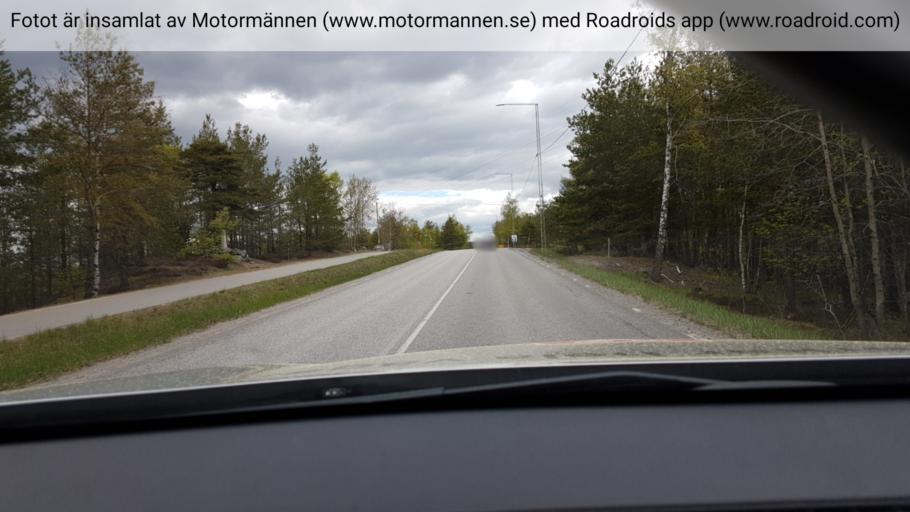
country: SE
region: Stockholm
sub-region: Haninge Kommun
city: Jordbro
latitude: 59.1289
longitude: 18.1161
